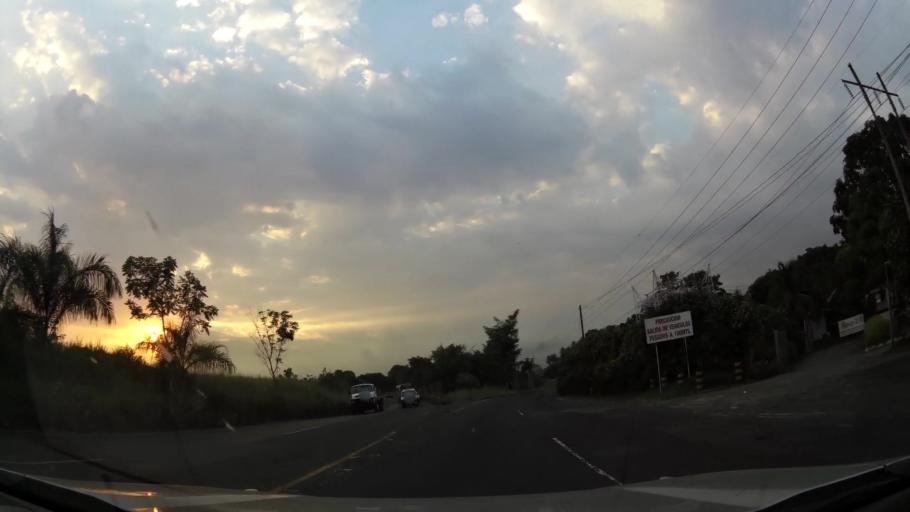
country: GT
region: Escuintla
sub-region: Municipio de La Democracia
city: La Democracia
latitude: 14.2751
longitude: -90.9136
